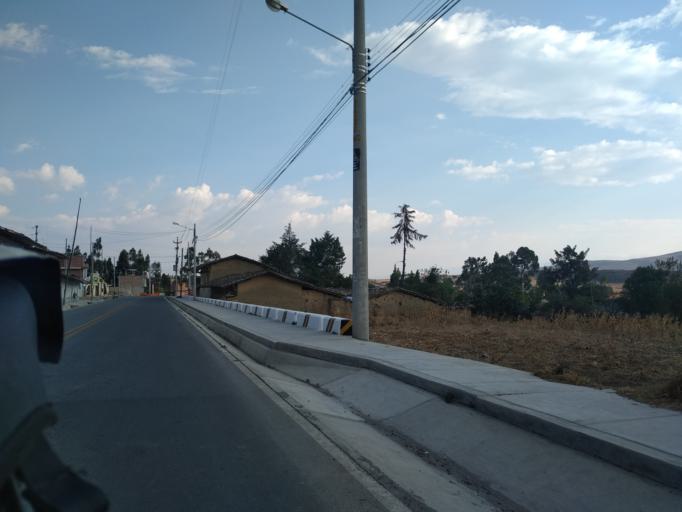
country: PE
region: Cajamarca
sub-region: San Marcos
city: La Grama
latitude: -7.3907
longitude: -78.1240
